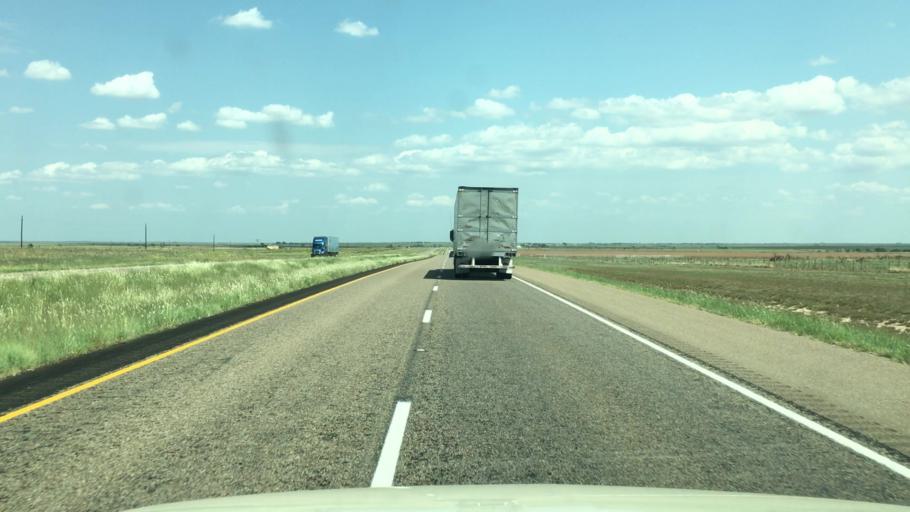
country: US
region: Texas
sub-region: Armstrong County
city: Claude
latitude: 35.0322
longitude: -101.1370
